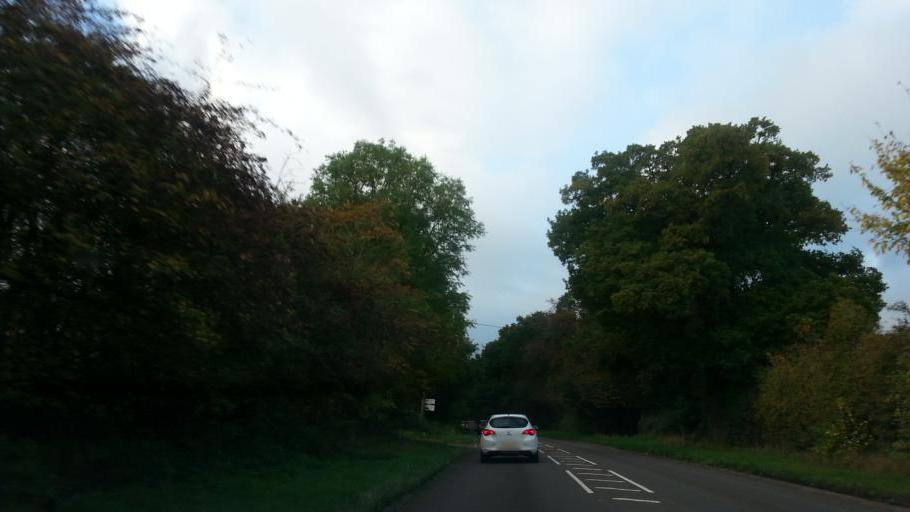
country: GB
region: England
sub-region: City and Borough of Birmingham
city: Sutton Coldfield
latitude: 52.5970
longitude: -1.7723
